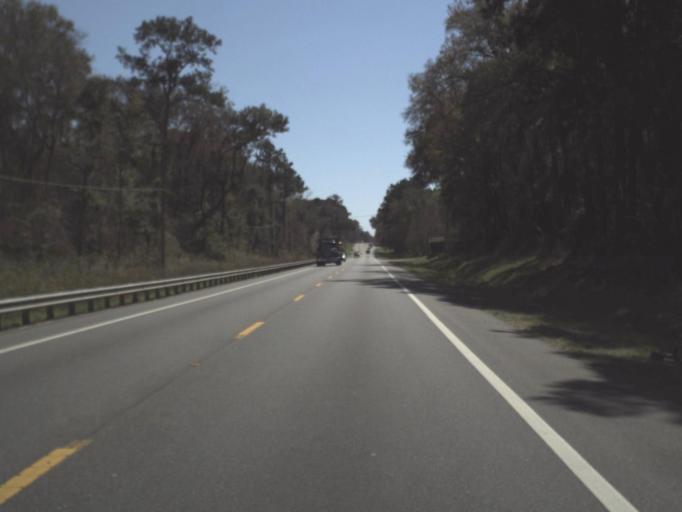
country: US
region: Florida
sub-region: Gadsden County
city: Midway
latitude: 30.5072
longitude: -84.3620
